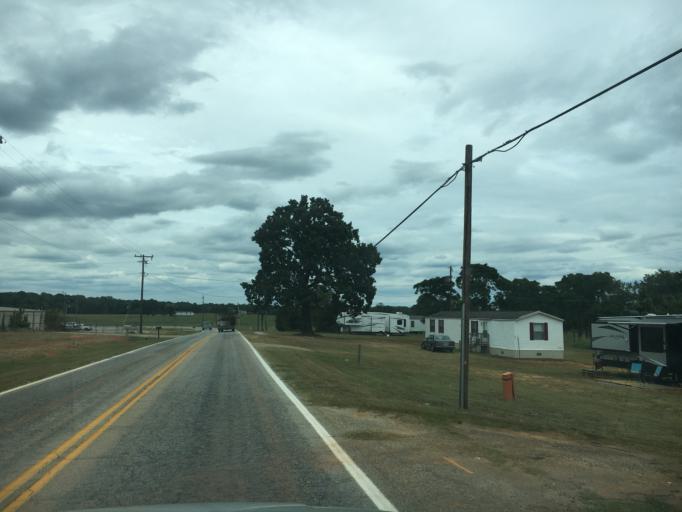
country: US
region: South Carolina
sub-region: Laurens County
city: Watts Mills
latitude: 34.4939
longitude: -81.9738
